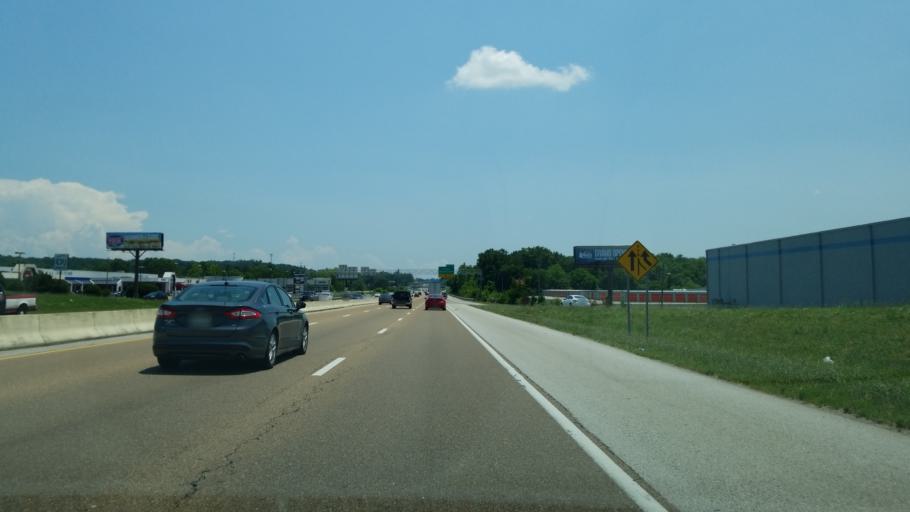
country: US
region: Tennessee
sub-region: Hamilton County
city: East Chattanooga
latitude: 35.0530
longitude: -85.1905
